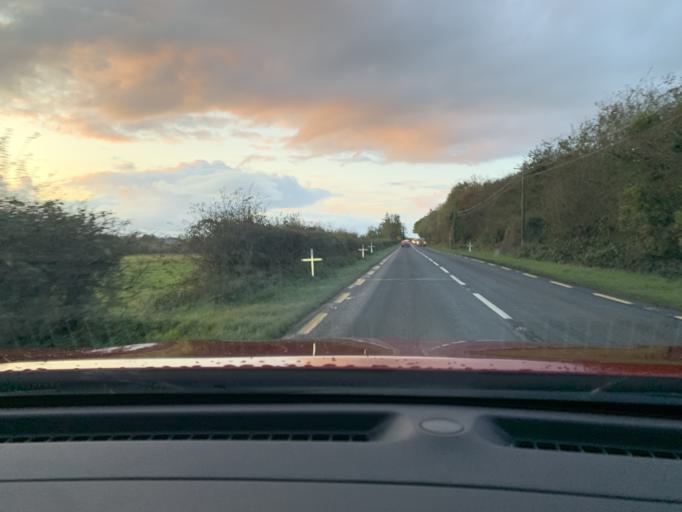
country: IE
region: Connaught
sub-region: Sligo
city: Collooney
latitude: 54.1395
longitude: -8.4536
